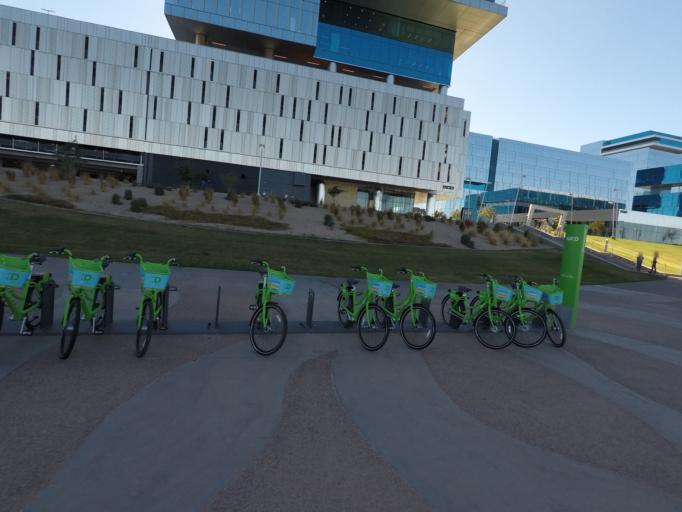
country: US
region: Arizona
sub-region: Maricopa County
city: Tempe Junction
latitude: 33.4306
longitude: -111.9301
